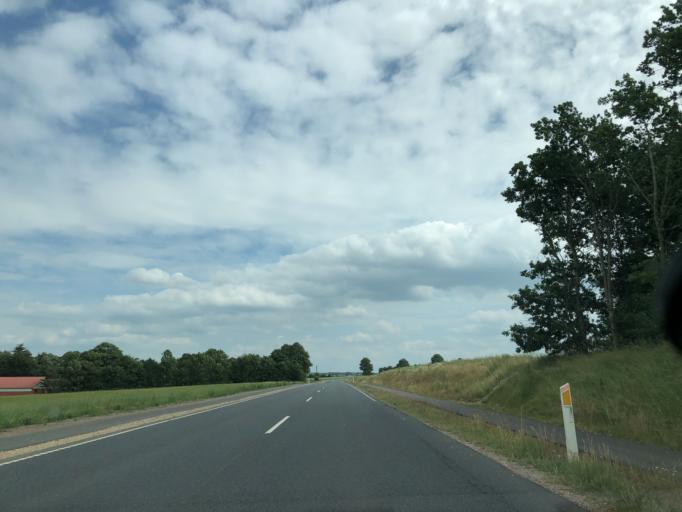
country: DK
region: Central Jutland
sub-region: Silkeborg Kommune
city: Svejbaek
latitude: 56.1861
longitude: 9.7102
